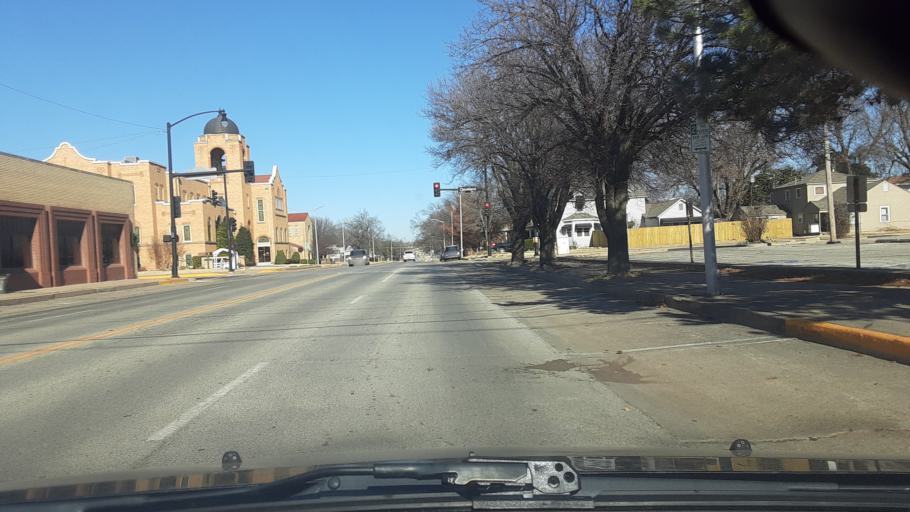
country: US
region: Oklahoma
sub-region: Kay County
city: Ponca City
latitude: 36.7041
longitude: -97.0786
